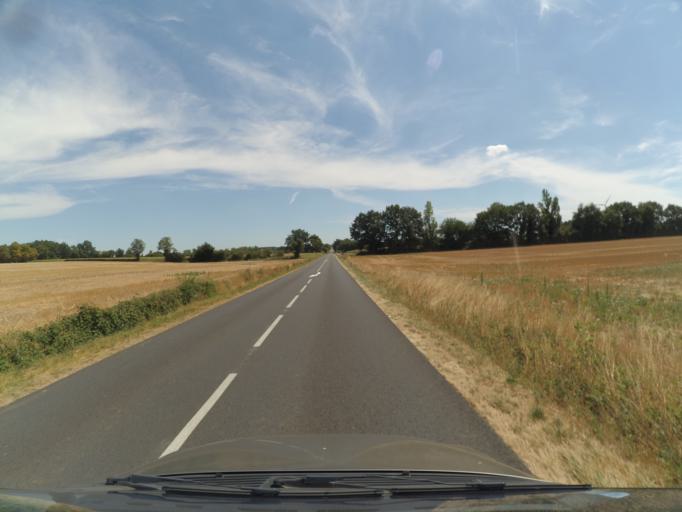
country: FR
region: Poitou-Charentes
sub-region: Departement de la Vienne
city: Saint-Maurice-la-Clouere
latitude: 46.3625
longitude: 0.4317
